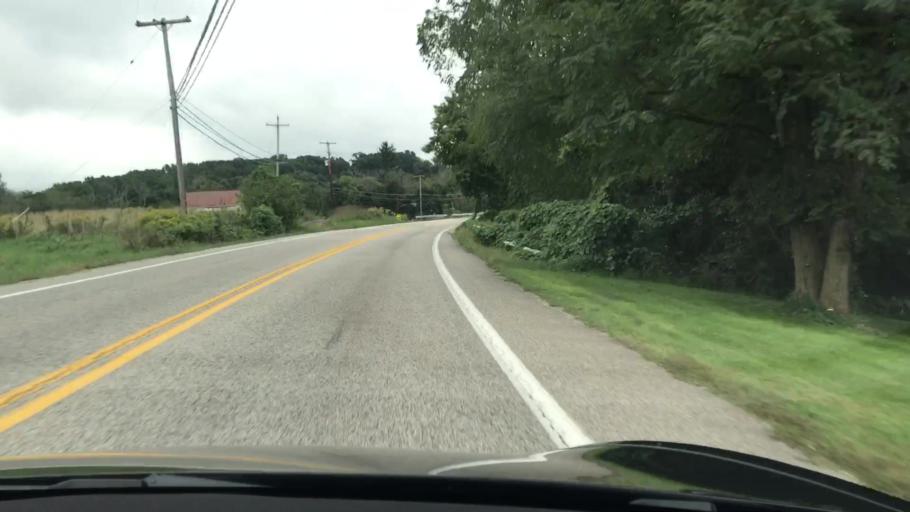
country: US
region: Pennsylvania
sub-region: Cumberland County
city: Shiremanstown
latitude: 40.1552
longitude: -76.9676
